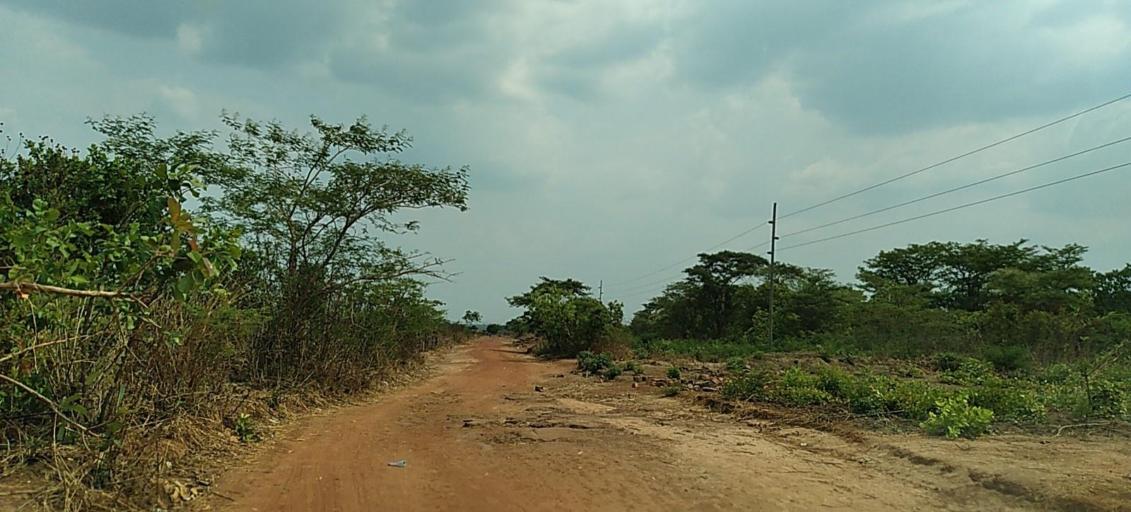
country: ZM
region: Copperbelt
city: Kalulushi
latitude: -12.8707
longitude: 28.0777
